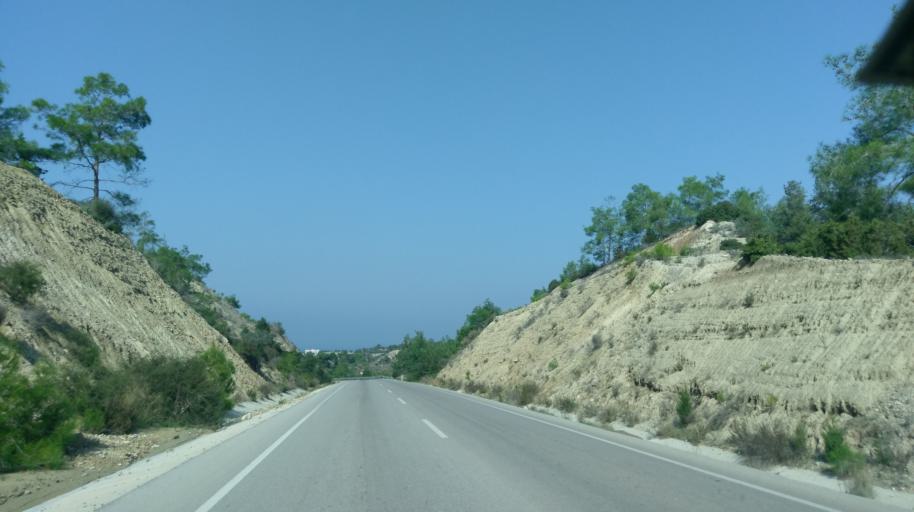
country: CY
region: Ammochostos
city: Lefkonoiko
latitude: 35.3594
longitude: 33.7118
